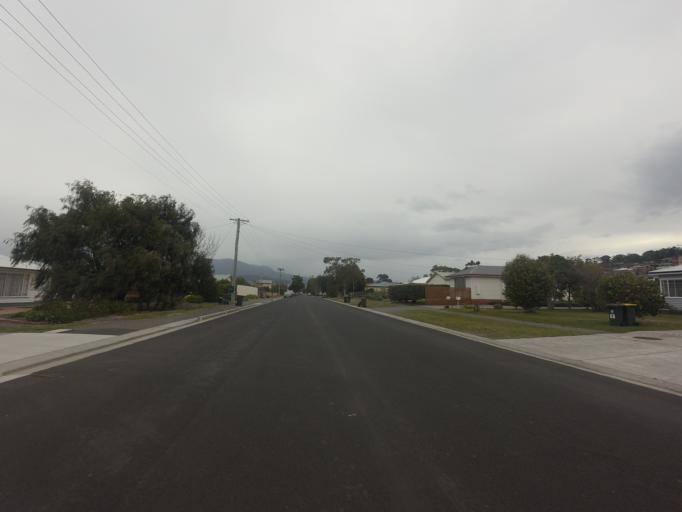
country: AU
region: Tasmania
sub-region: Clarence
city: Bellerive
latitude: -42.8785
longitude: 147.3876
